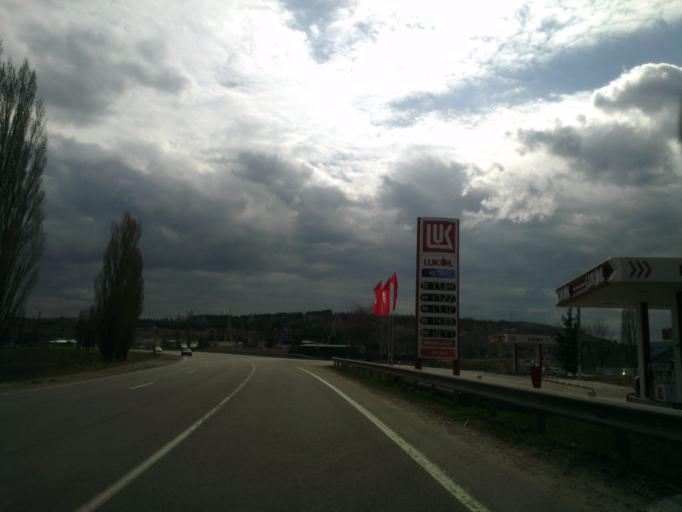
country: MD
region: Laloveni
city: Ialoveni
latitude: 46.9121
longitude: 28.6880
